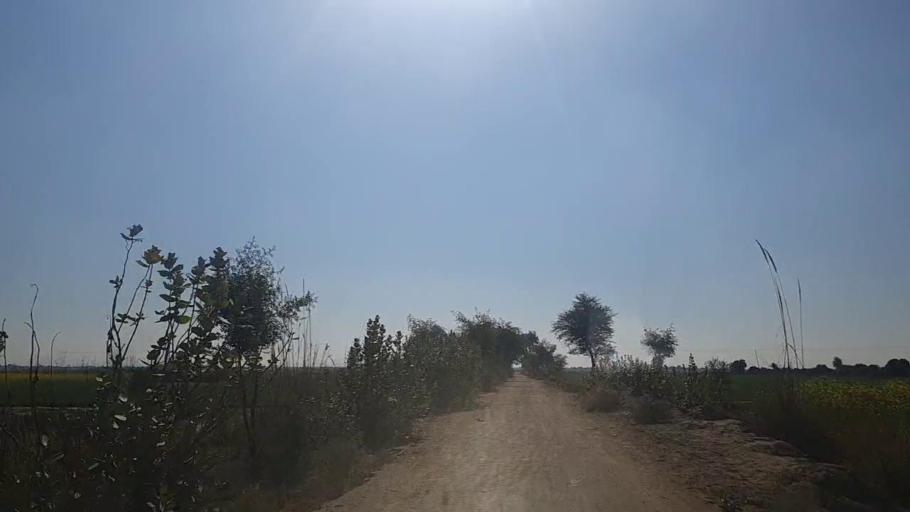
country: PK
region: Sindh
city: Sinjhoro
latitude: 26.1574
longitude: 68.8602
